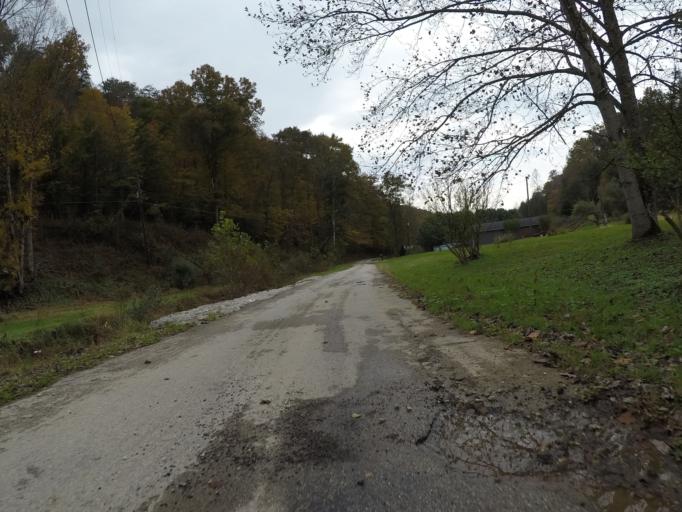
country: US
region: West Virginia
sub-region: Wayne County
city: Lavalette
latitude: 38.3547
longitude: -82.4187
